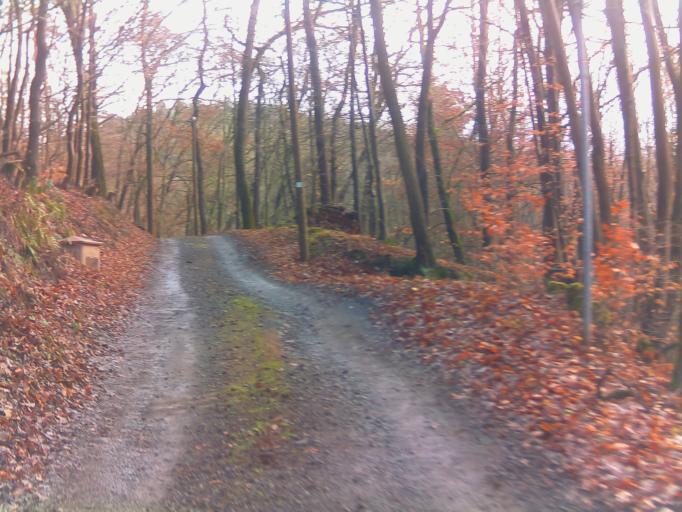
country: DE
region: Thuringia
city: Hummelshain
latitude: 50.7447
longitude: 11.6420
